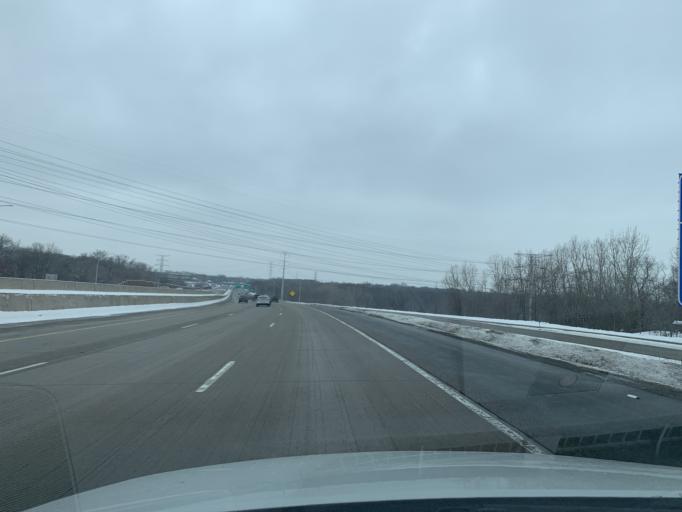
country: US
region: Minnesota
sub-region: Anoka County
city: Coon Rapids
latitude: 45.1372
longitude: -93.2930
